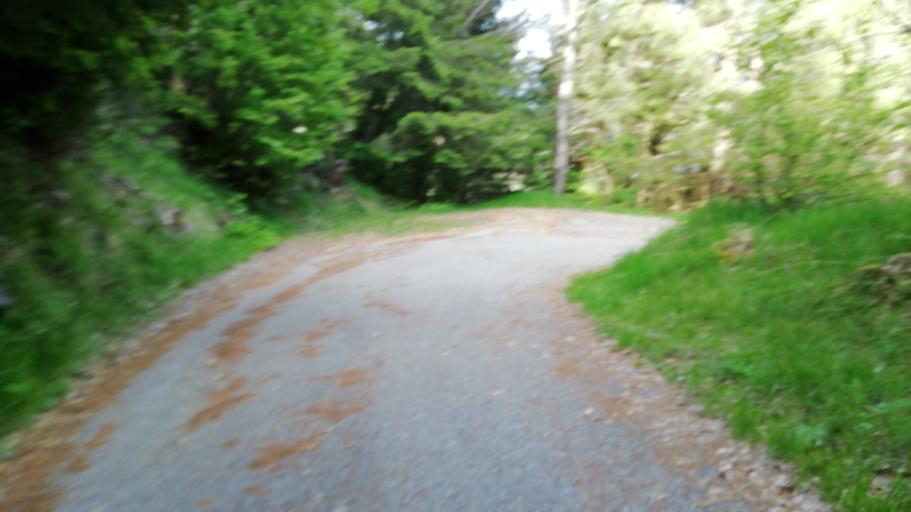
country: IT
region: Veneto
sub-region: Provincia di Belluno
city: Valle di Cadore
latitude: 46.4256
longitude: 12.3206
